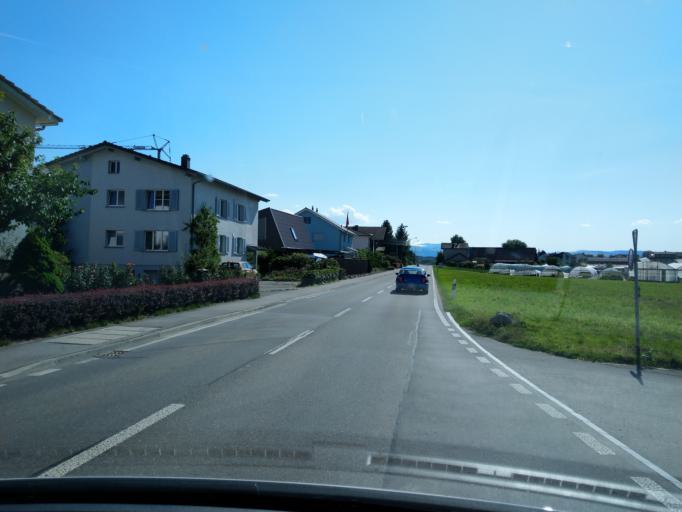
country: CH
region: Lucerne
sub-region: Hochdorf District
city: Emmen
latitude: 47.1019
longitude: 8.2846
